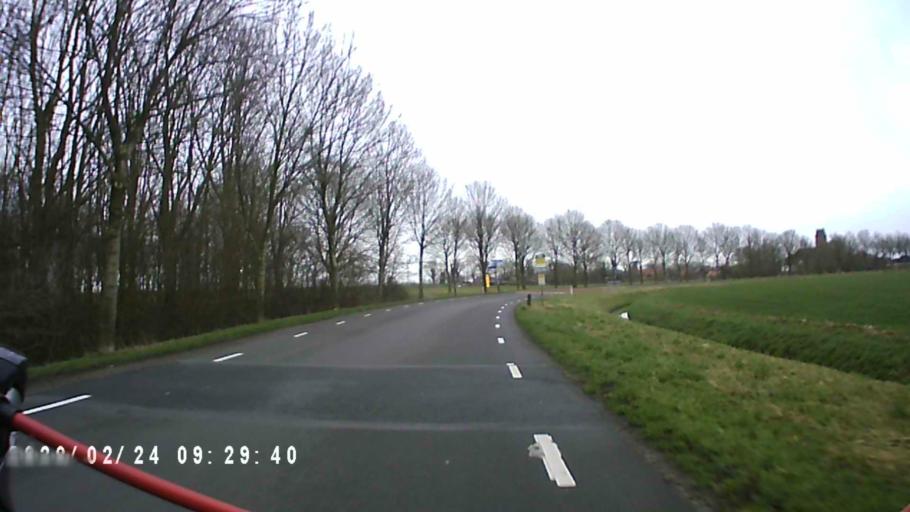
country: NL
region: Groningen
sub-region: Gemeente Winsum
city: Winsum
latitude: 53.3078
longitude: 6.4867
